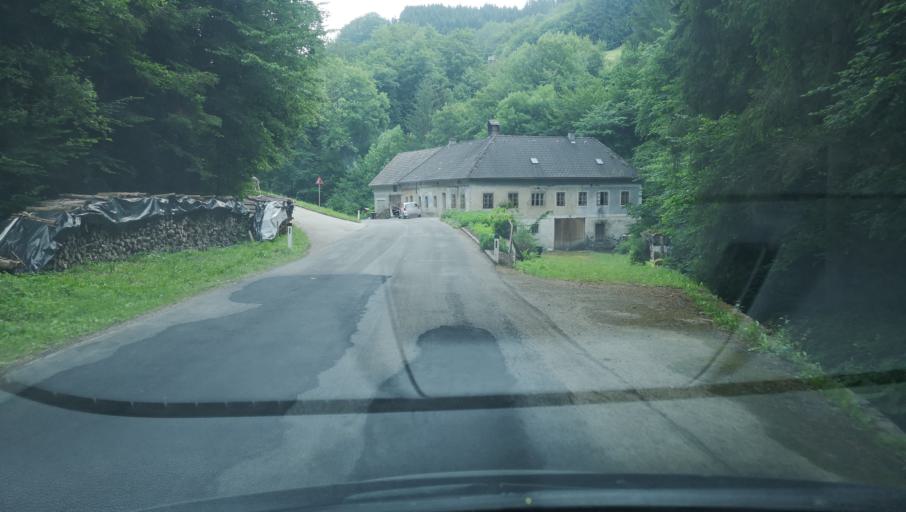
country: AT
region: Lower Austria
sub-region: Politischer Bezirk Melk
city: Nochling
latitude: 48.1860
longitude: 14.9782
